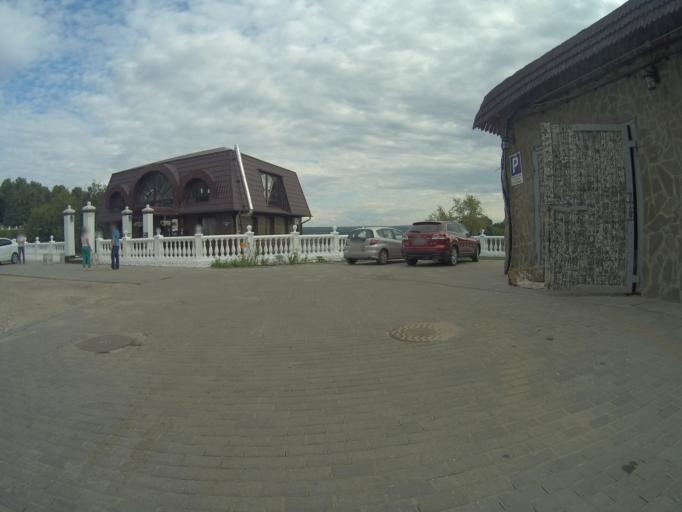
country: RU
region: Vladimir
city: Vladimir
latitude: 56.1277
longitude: 40.4052
